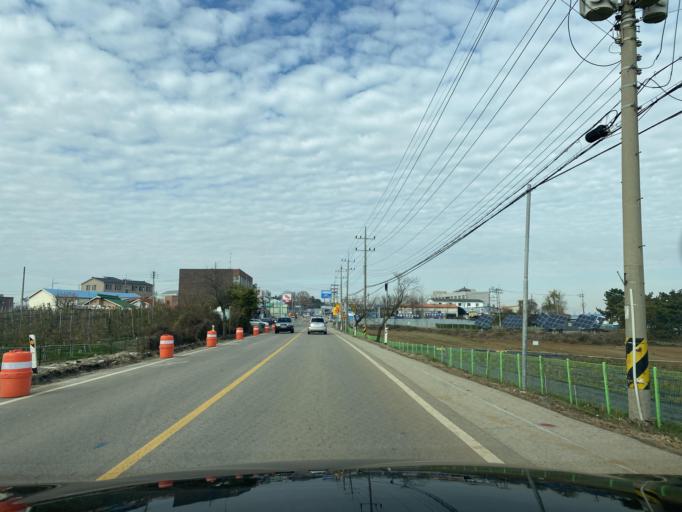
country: KR
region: Chungcheongnam-do
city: Yesan
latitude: 36.6867
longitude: 126.8005
